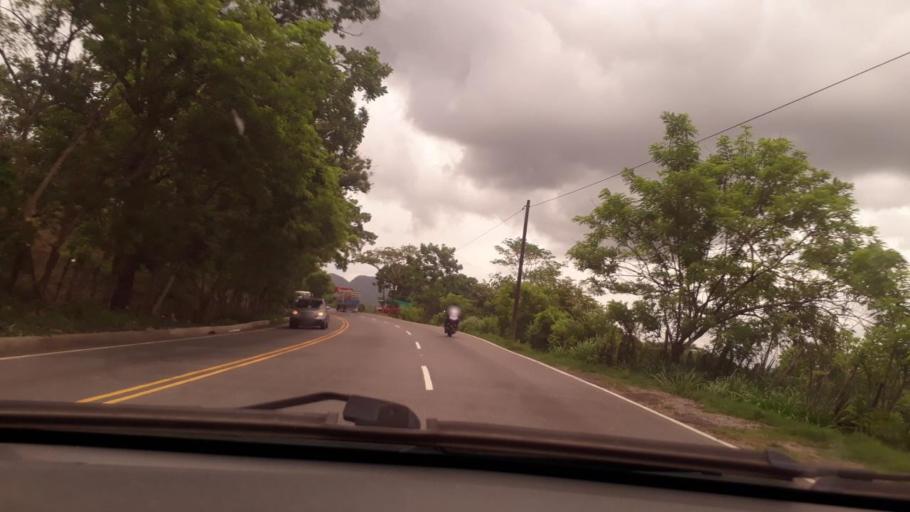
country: GT
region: Izabal
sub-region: Municipio de Los Amates
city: Los Amates
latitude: 15.2238
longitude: -89.2155
